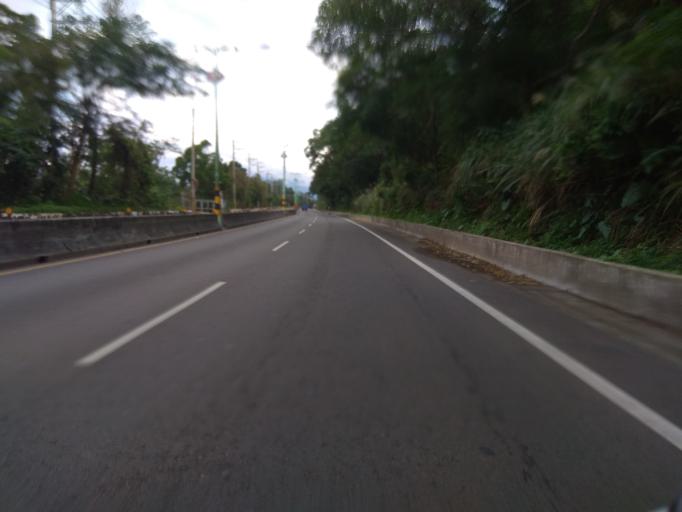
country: TW
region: Taiwan
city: Daxi
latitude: 24.8479
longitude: 121.2076
